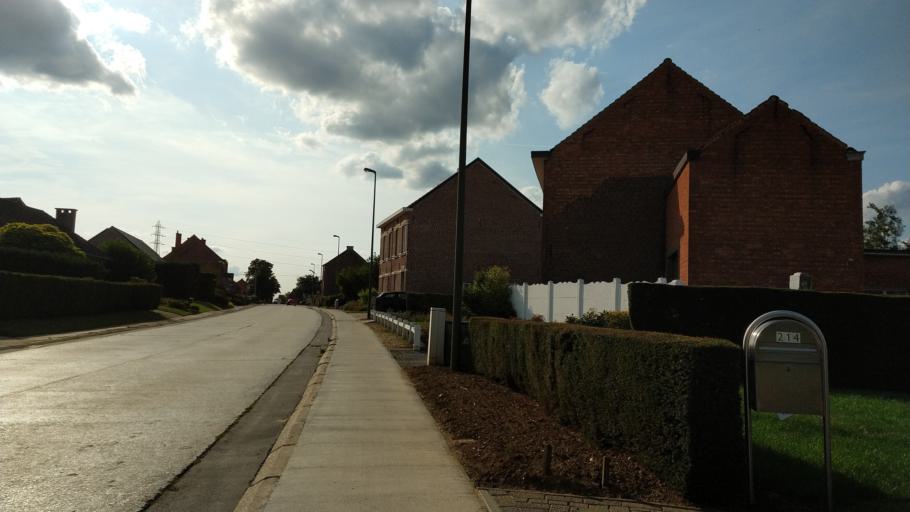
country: BE
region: Flanders
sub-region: Provincie Vlaams-Brabant
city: Holsbeek
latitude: 50.8759
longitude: 4.7653
